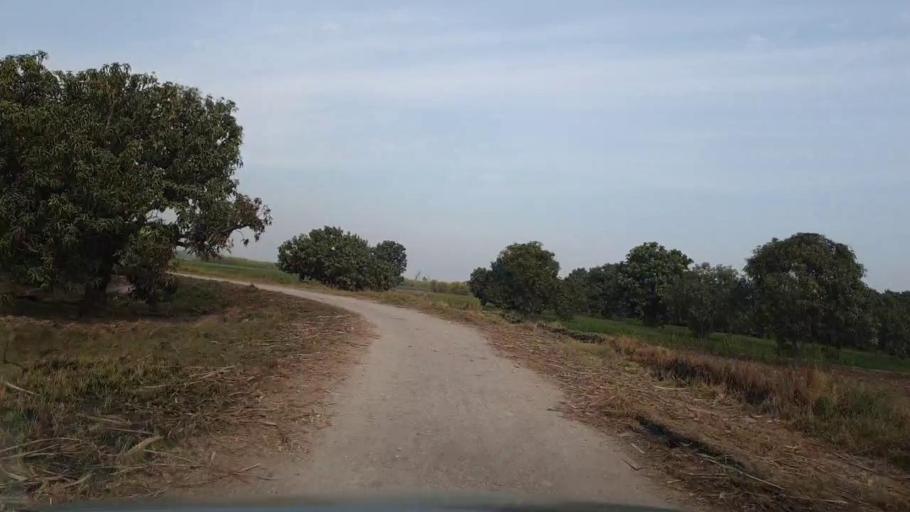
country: PK
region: Sindh
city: Matiari
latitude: 25.5620
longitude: 68.5410
